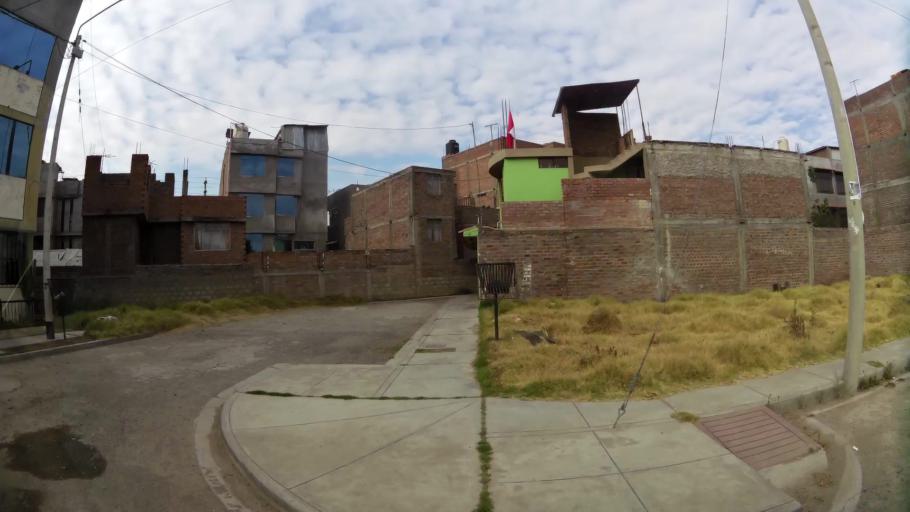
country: PE
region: Junin
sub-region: Provincia de Huancayo
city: Huancayo
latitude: -12.0492
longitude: -75.1945
